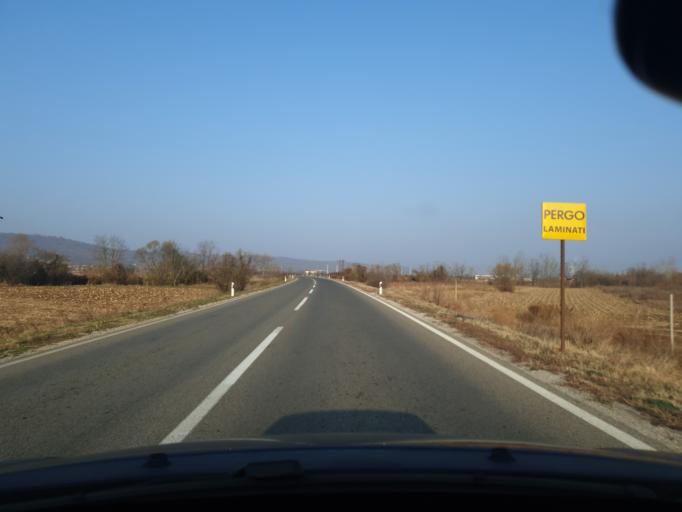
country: RS
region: Central Serbia
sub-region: Jablanicki Okrug
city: Leskovac
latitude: 42.9354
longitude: 22.0093
